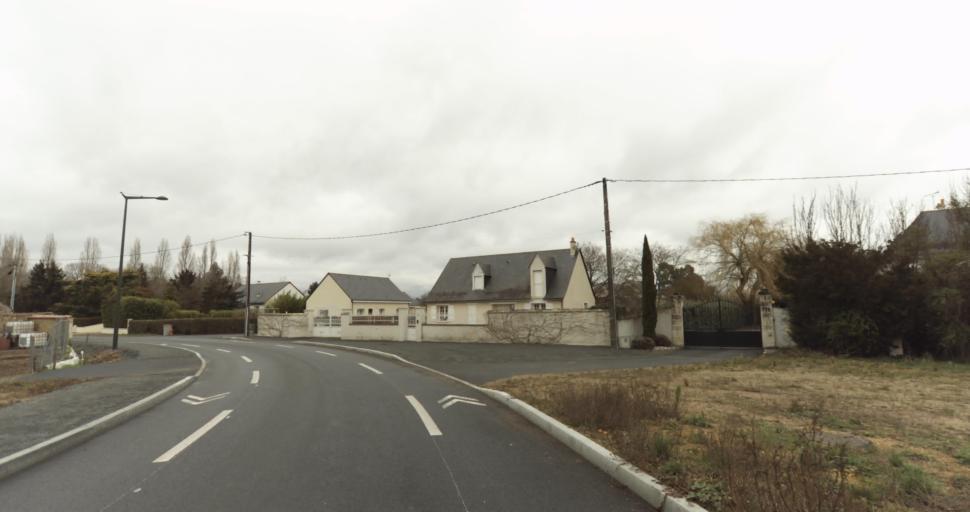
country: FR
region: Pays de la Loire
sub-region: Departement de Maine-et-Loire
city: Distre
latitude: 47.2463
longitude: -0.1080
